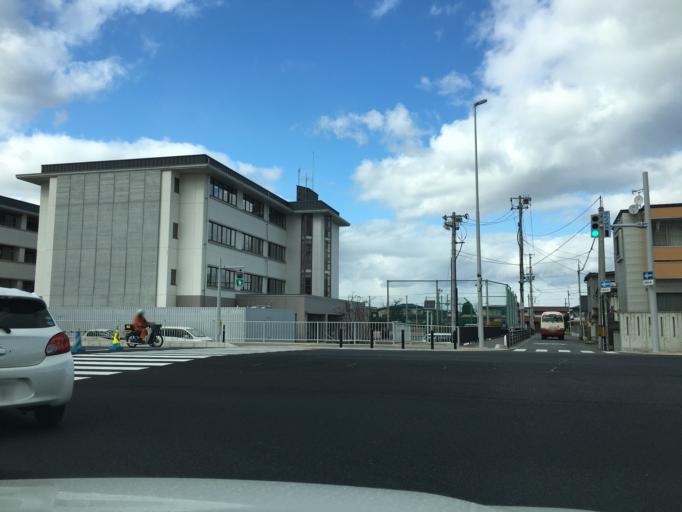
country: JP
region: Yamagata
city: Yamagata-shi
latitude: 38.2596
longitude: 140.3283
